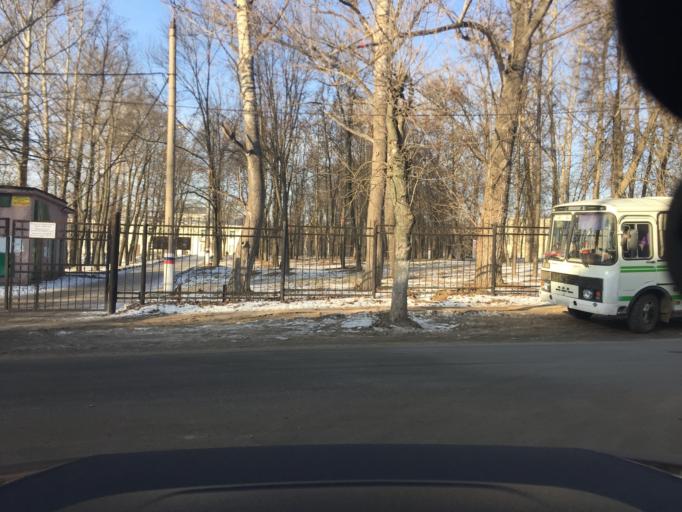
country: RU
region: Tula
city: Tula
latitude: 54.1837
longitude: 37.7028
